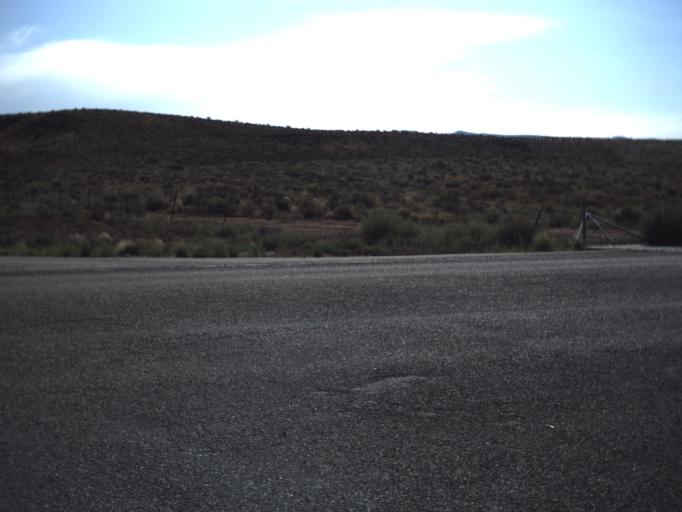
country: US
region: Utah
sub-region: Washington County
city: Saint George
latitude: 37.0002
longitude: -113.5604
